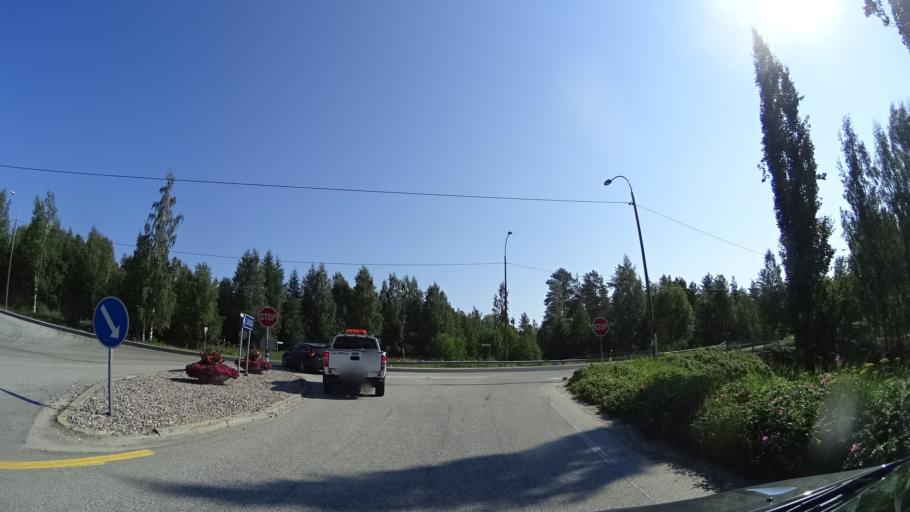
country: FI
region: North Karelia
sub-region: Joensuu
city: Juuka
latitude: 63.2468
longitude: 29.2667
